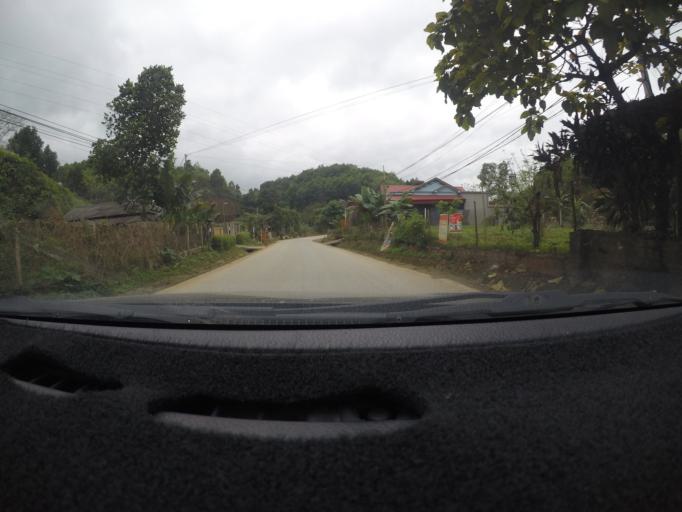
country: VN
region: Yen Bai
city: Co Phuc
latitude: 21.9165
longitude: 104.8082
